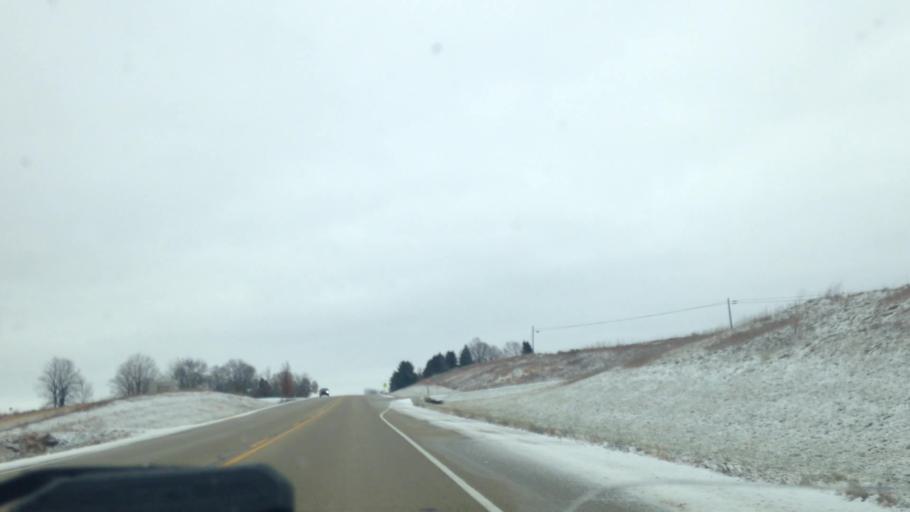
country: US
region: Wisconsin
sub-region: Dodge County
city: Horicon
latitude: 43.4714
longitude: -88.6033
